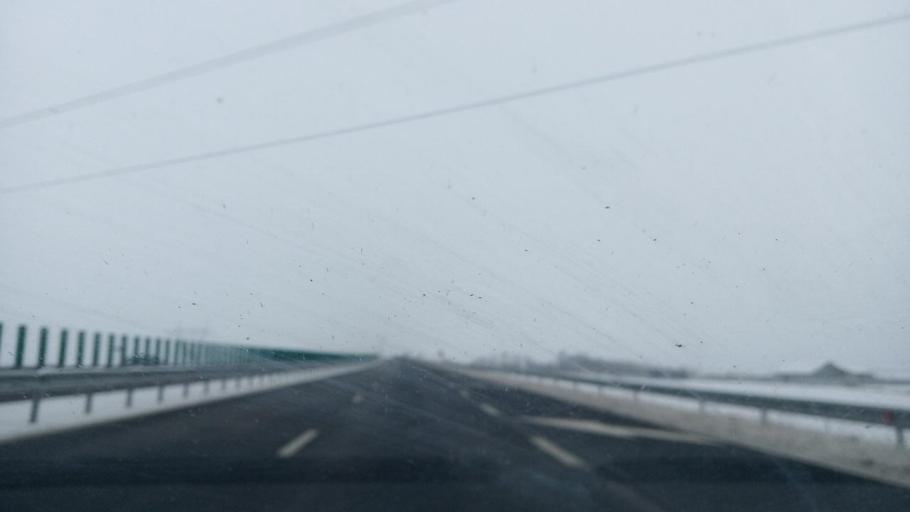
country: RO
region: Bacau
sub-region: Comuna Letea Veche
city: Holt
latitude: 46.5969
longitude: 26.9606
